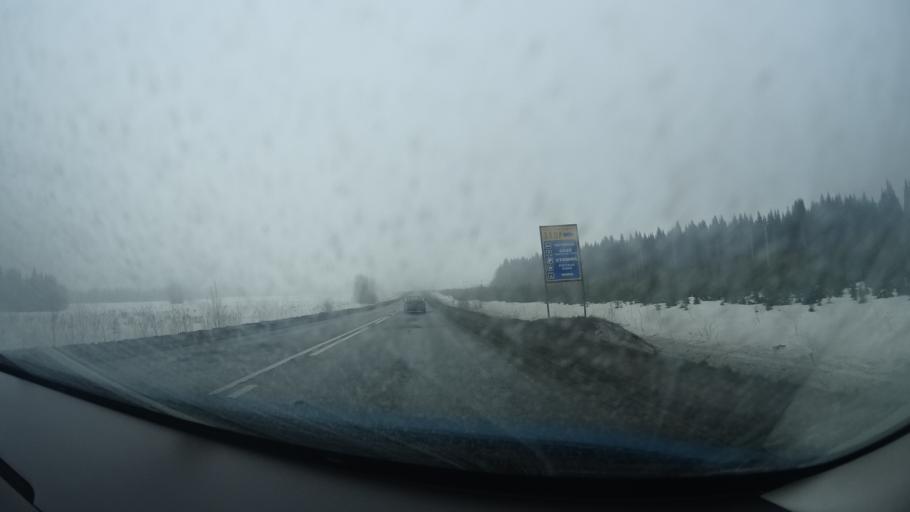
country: RU
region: Perm
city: Kuyeda
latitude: 56.4700
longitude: 55.6997
